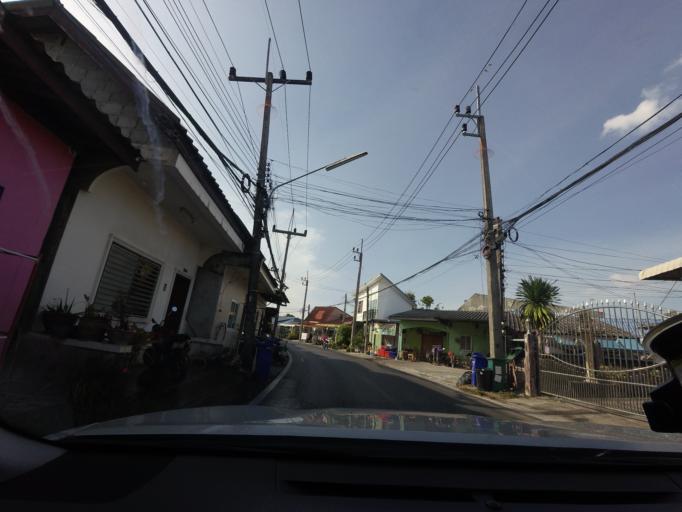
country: TH
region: Phuket
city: Thalang
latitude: 8.0166
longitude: 98.3180
